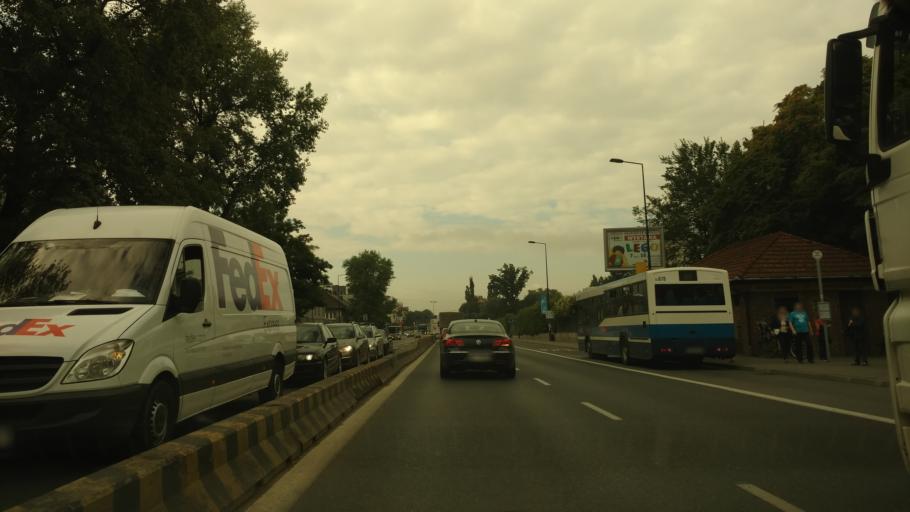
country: PL
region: Lesser Poland Voivodeship
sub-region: Krakow
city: Krakow
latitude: 50.0850
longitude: 19.9537
